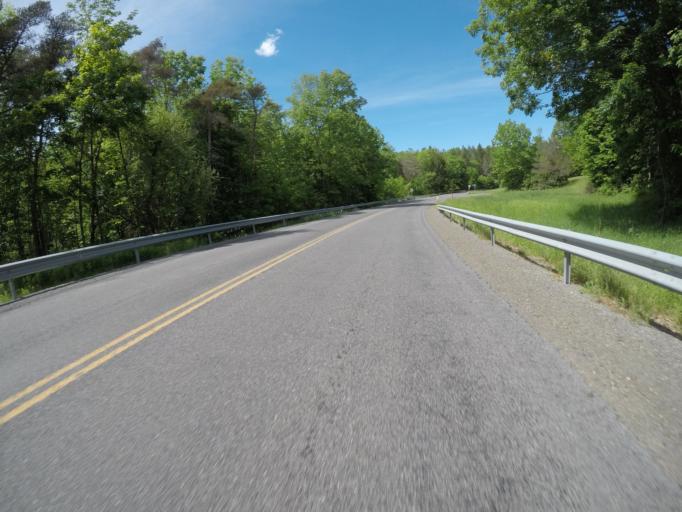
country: US
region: New York
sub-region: Delaware County
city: Delhi
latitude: 42.1186
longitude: -74.8207
